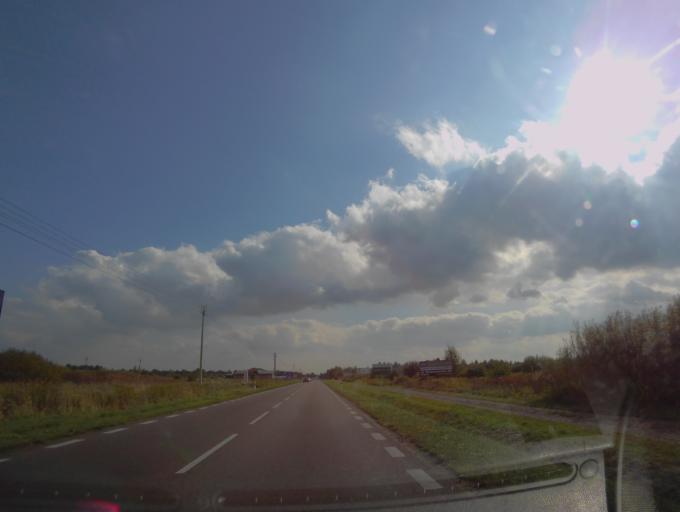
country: PL
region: Lublin Voivodeship
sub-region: Powiat bilgorajski
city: Bilgoraj
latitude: 50.5613
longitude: 22.6960
